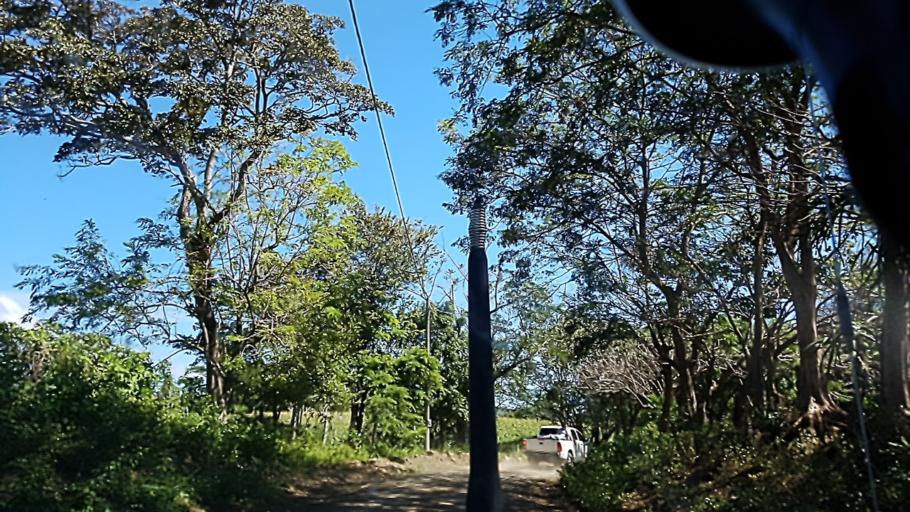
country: NI
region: Carazo
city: Santa Teresa
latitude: 11.7129
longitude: -86.1754
